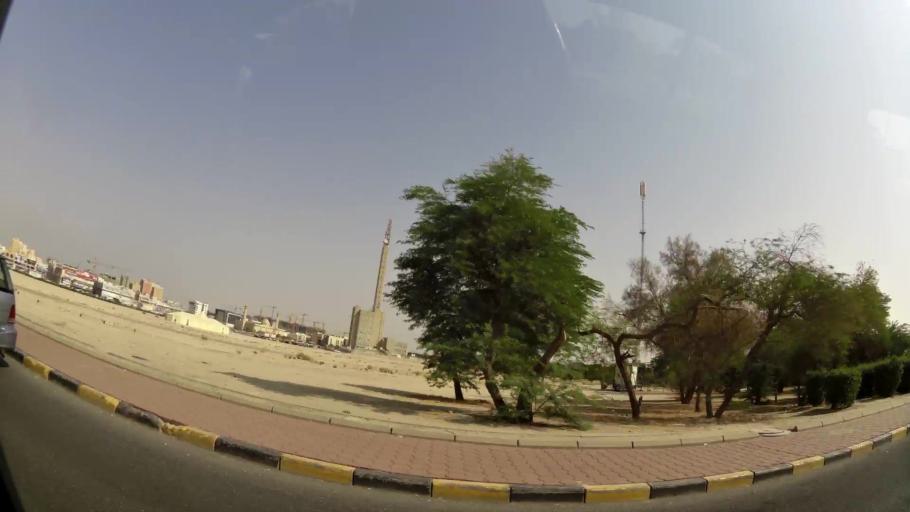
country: KW
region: Muhafazat al Jahra'
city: Al Jahra'
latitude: 29.3372
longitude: 47.6669
